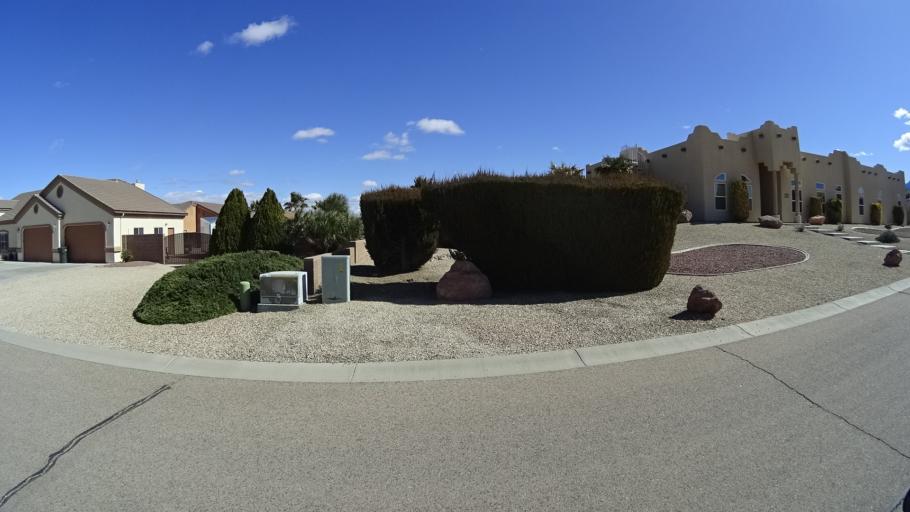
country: US
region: Arizona
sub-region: Mohave County
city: Kingman
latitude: 35.2069
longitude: -113.9696
